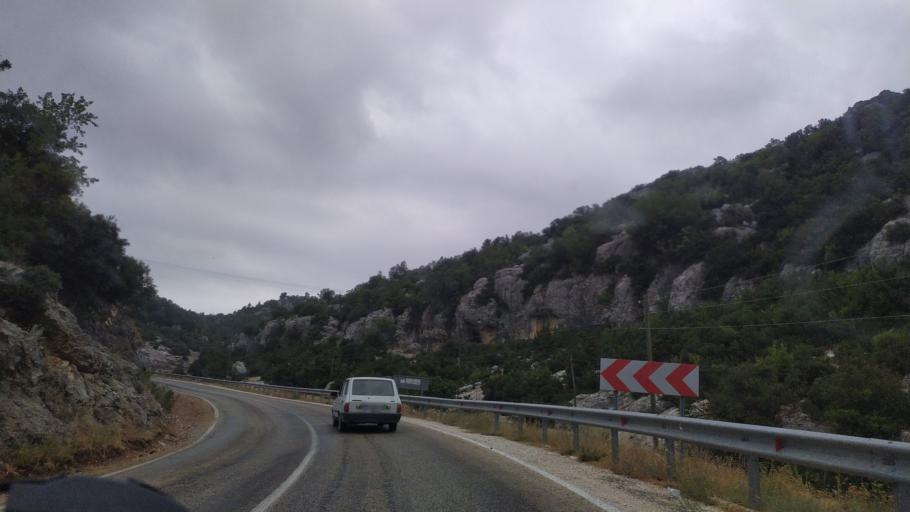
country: TR
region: Mersin
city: Silifke
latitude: 36.5317
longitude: 33.9443
